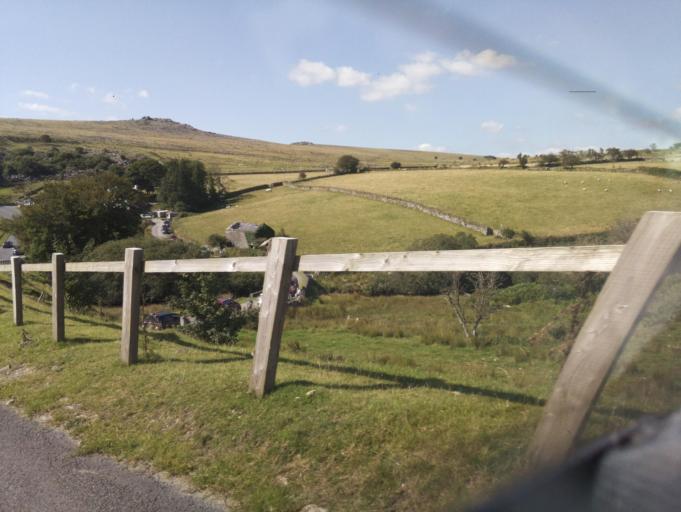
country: GB
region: England
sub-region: Devon
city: Horrabridge
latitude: 50.5570
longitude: -4.0478
